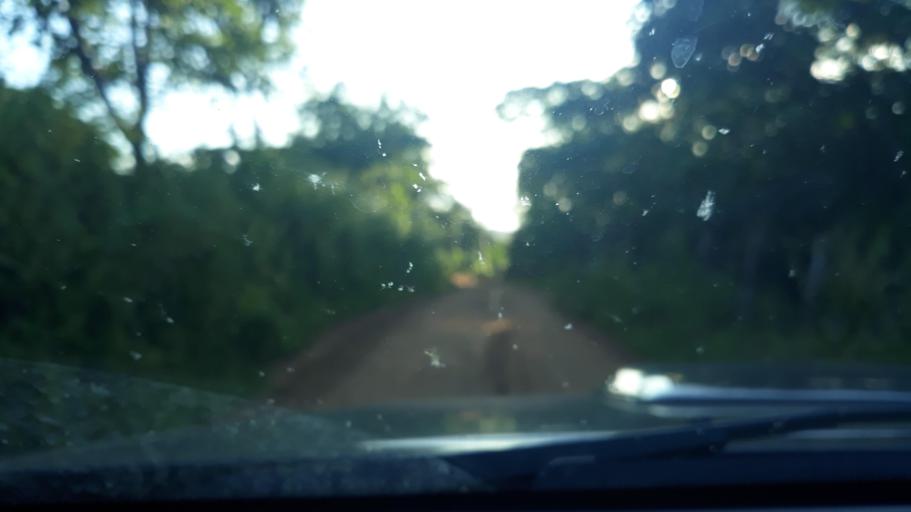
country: BR
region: Bahia
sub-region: Riacho De Santana
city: Riacho de Santana
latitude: -13.8434
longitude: -42.7392
